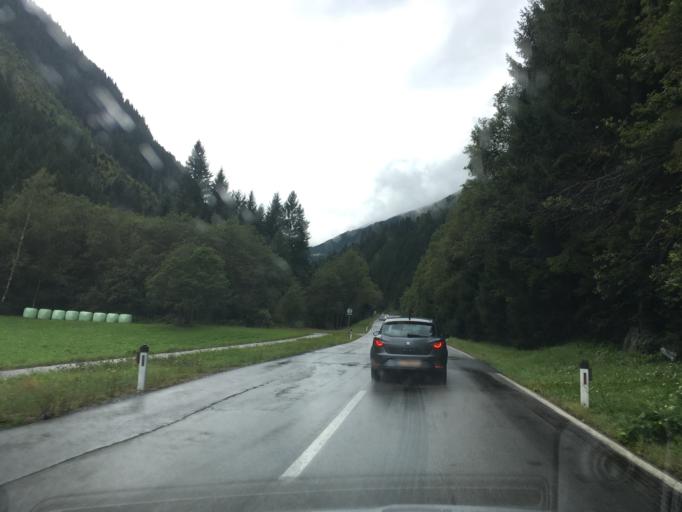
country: AT
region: Tyrol
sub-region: Politischer Bezirk Lienz
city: Hopfgarten in Defereggen
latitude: 46.9254
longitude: 12.4706
